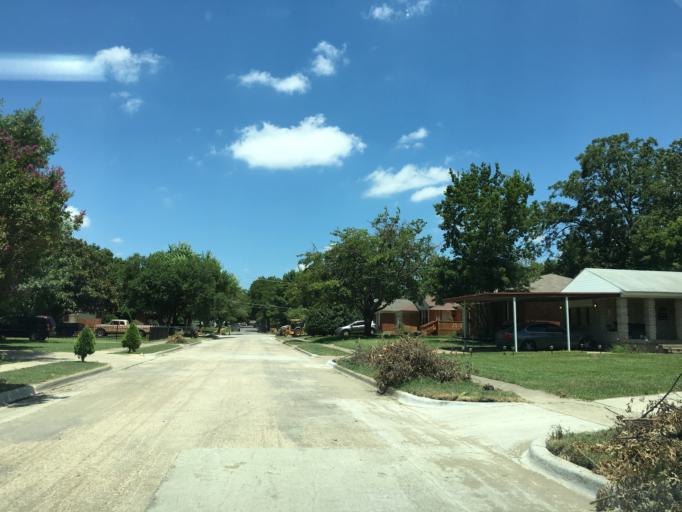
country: US
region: Texas
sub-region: Dallas County
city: Garland
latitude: 32.8452
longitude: -96.6720
